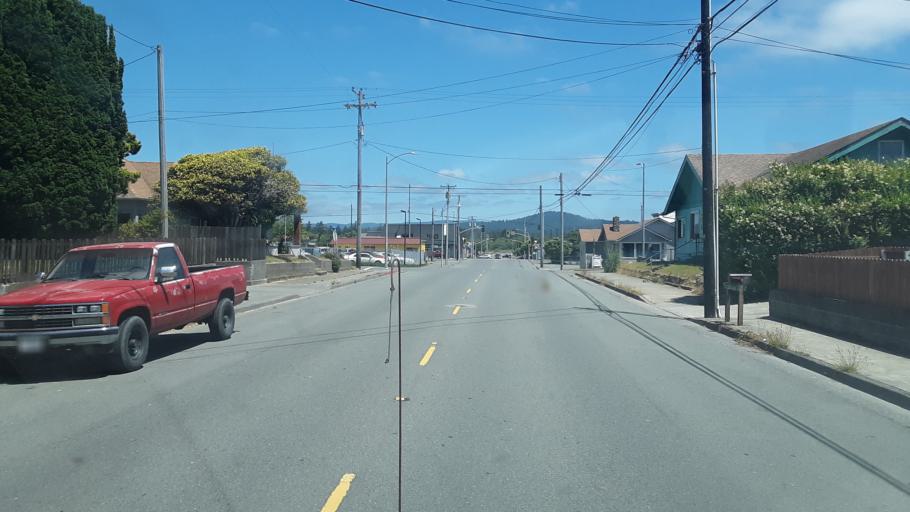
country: US
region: California
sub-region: Del Norte County
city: Crescent City
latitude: 41.7546
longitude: -124.1971
